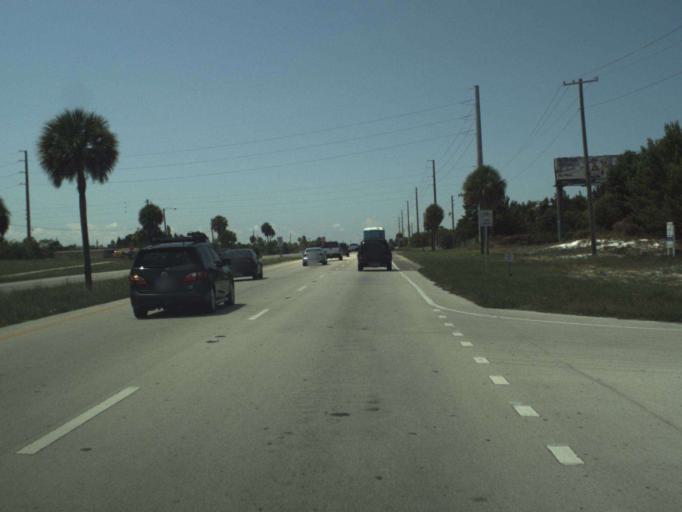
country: US
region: Florida
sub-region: Saint Lucie County
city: Fort Pierce North
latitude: 27.4716
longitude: -80.3346
